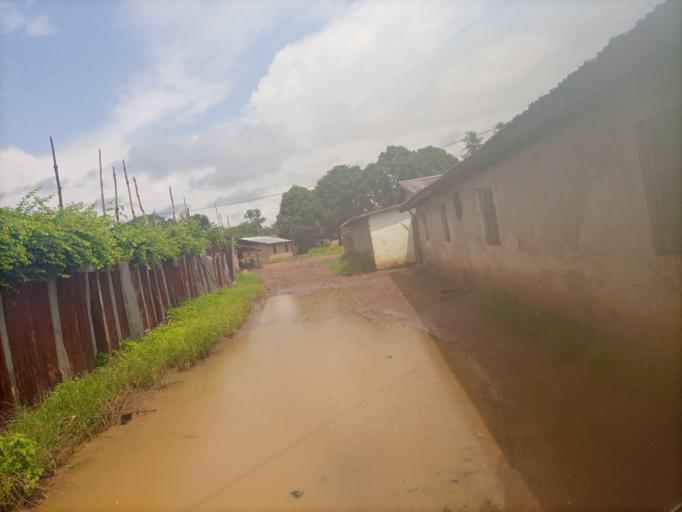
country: SL
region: Northern Province
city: Tintafor
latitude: 8.6322
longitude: -13.2164
